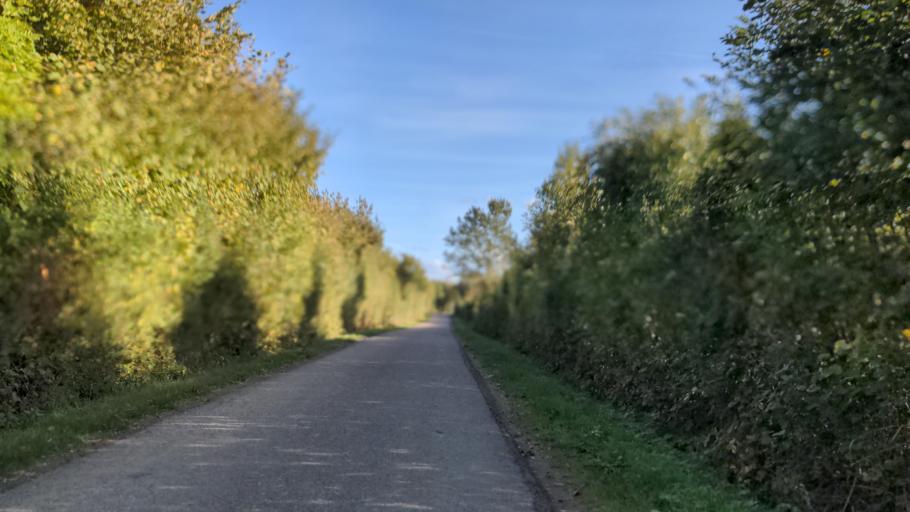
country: DE
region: Schleswig-Holstein
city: Manhagen
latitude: 54.1698
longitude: 10.9073
